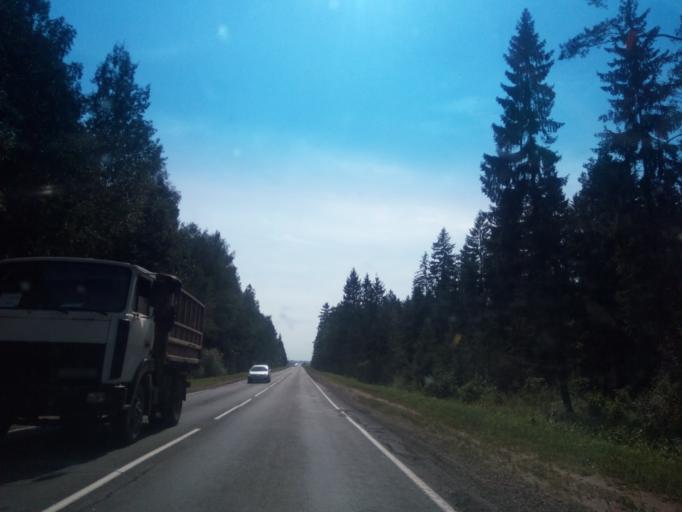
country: BY
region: Vitebsk
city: Vyerkhnyadzvinsk
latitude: 55.7900
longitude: 27.9712
